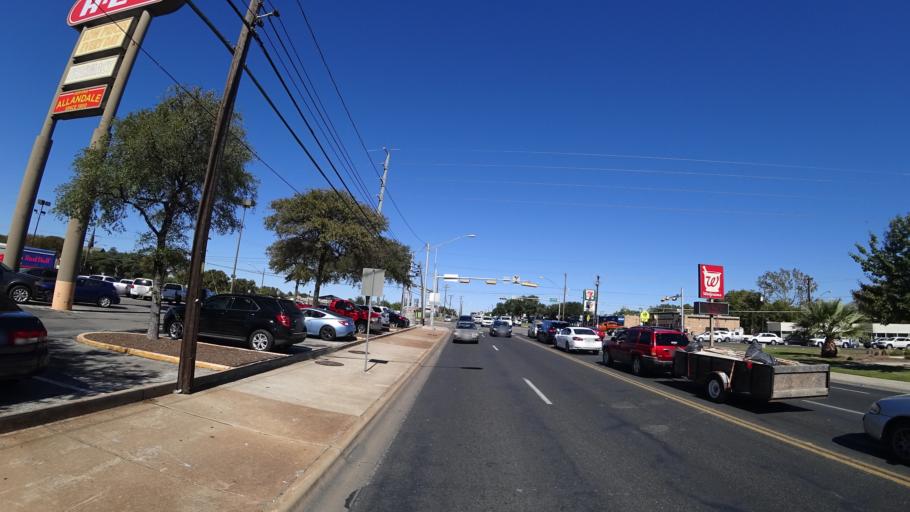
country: US
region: Texas
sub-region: Travis County
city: Austin
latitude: 30.3343
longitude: -97.7400
